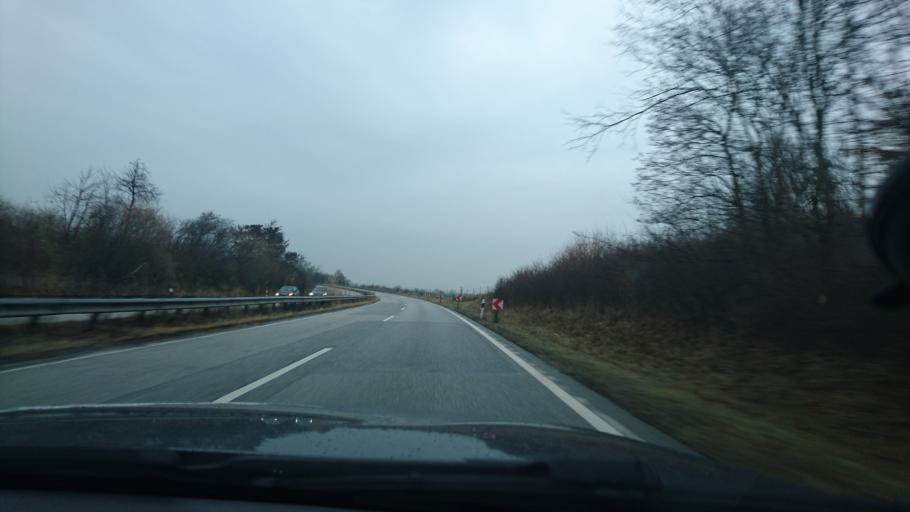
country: DE
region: Schleswig-Holstein
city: Damlos
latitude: 54.2627
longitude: 10.8898
